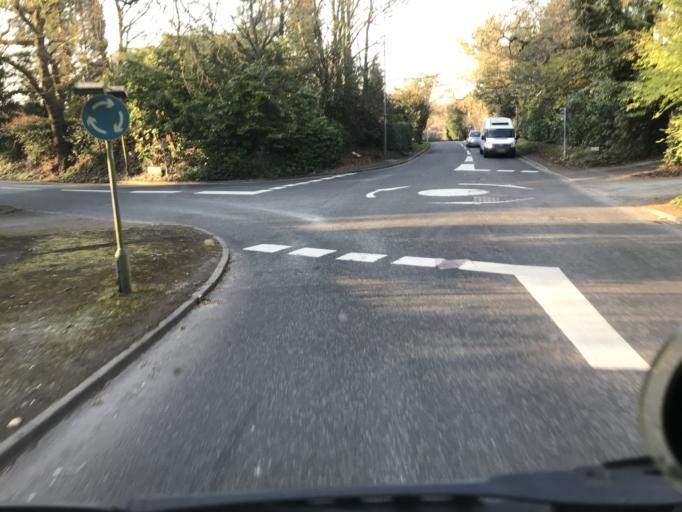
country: GB
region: England
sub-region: Cheshire East
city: Wilmslow
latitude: 53.3231
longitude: -2.2133
